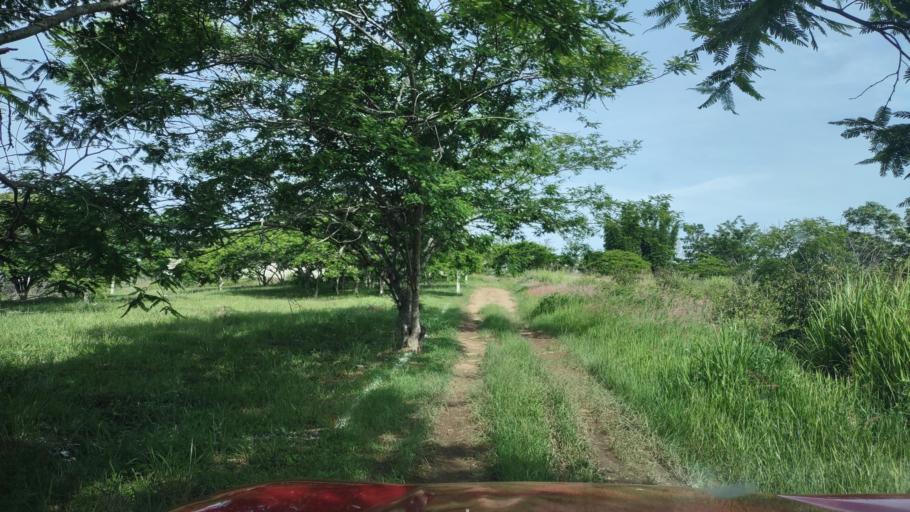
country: MX
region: Veracruz
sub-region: Emiliano Zapata
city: Dos Rios
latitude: 19.4760
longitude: -96.8286
